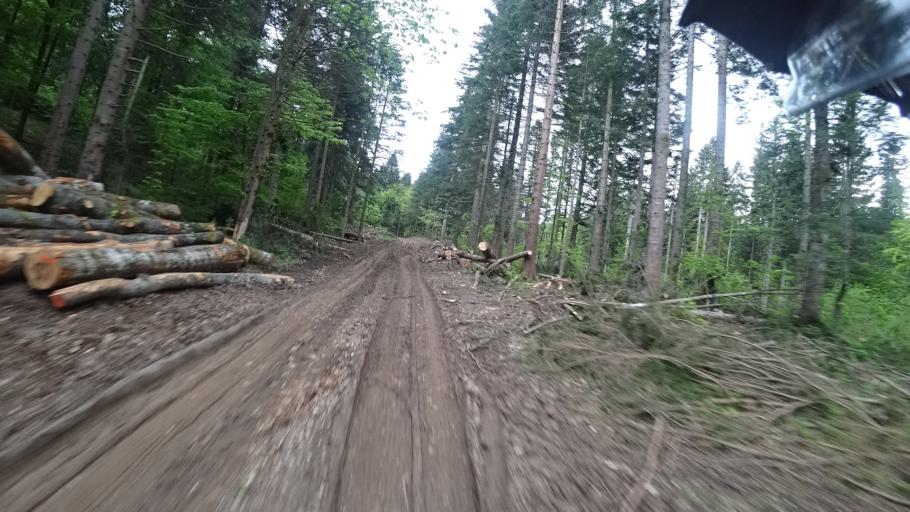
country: HR
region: Karlovacka
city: Plaski
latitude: 44.9518
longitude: 15.4151
